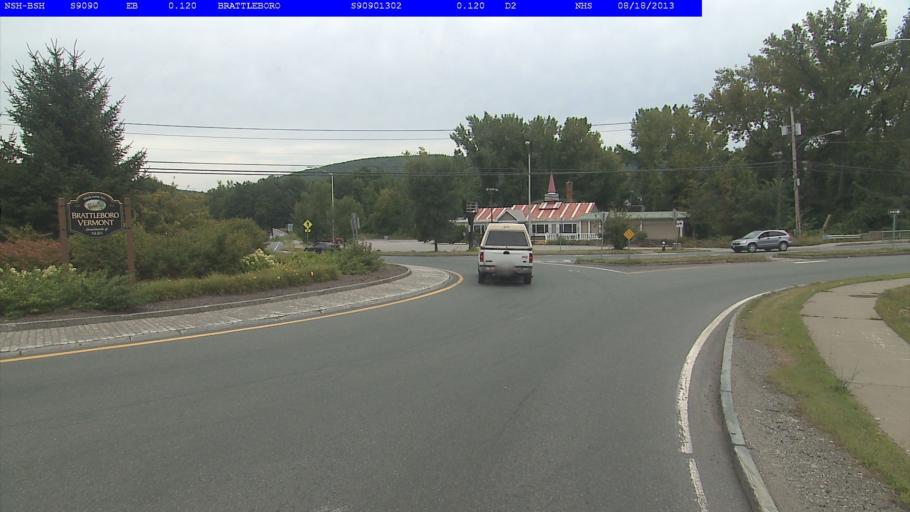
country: US
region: Vermont
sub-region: Windham County
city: Brattleboro
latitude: 42.8850
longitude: -72.5570
